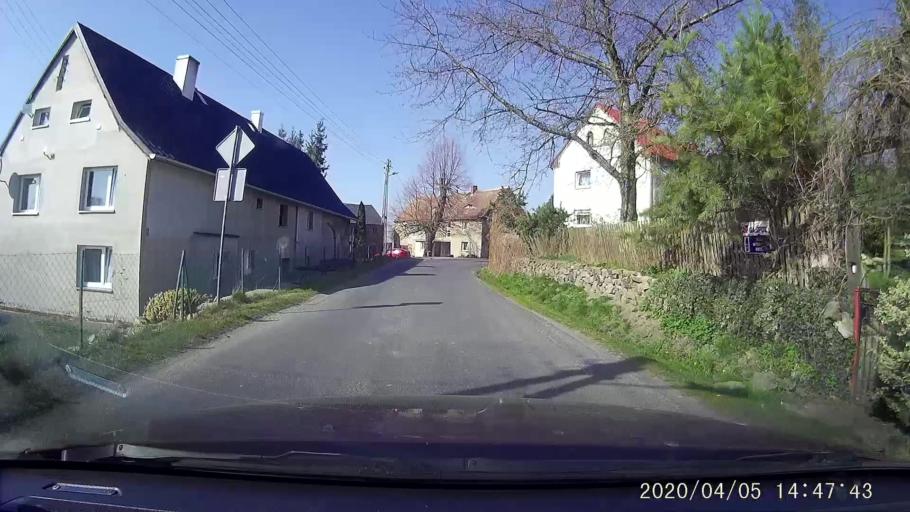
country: PL
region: Lower Silesian Voivodeship
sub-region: Powiat zgorzelecki
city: Sulikow
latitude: 51.0654
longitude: 15.1058
